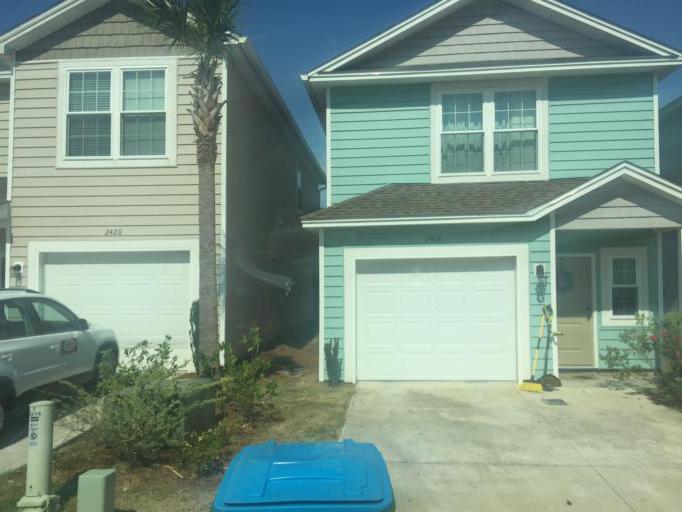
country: US
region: Florida
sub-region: Bay County
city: Lower Grand Lagoon
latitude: 30.1596
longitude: -85.7576
